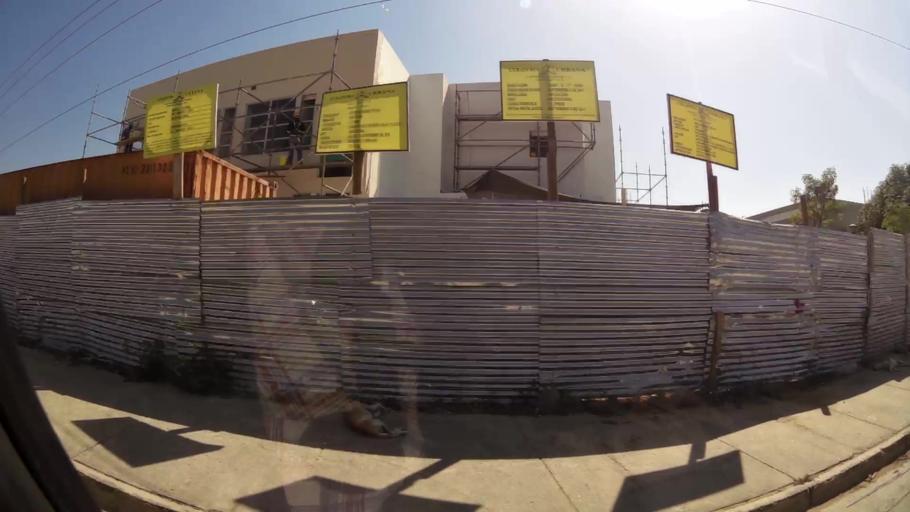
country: CO
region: Bolivar
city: Cartagena
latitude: 10.4411
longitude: -75.5264
